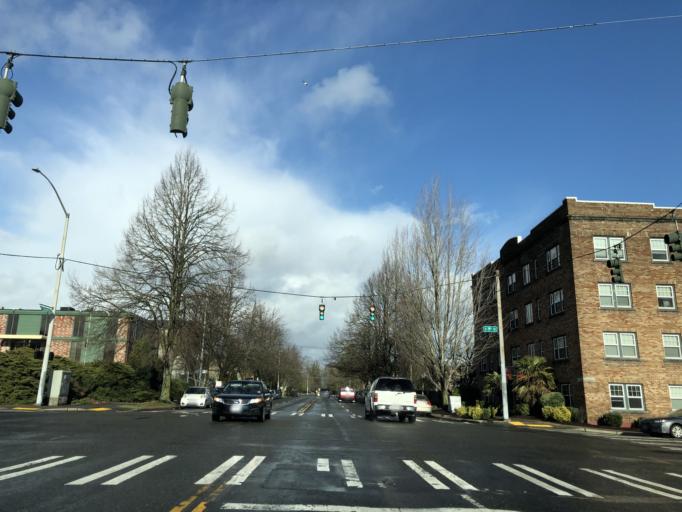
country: US
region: Washington
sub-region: Pierce County
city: Tacoma
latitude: 47.2542
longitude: -122.4478
